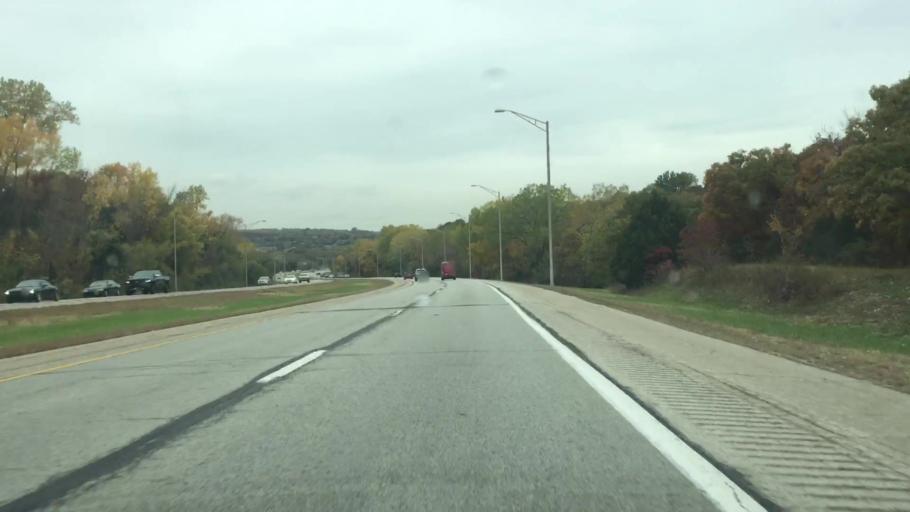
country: US
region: Kansas
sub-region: Wyandotte County
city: Edwardsville
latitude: 39.0107
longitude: -94.7980
